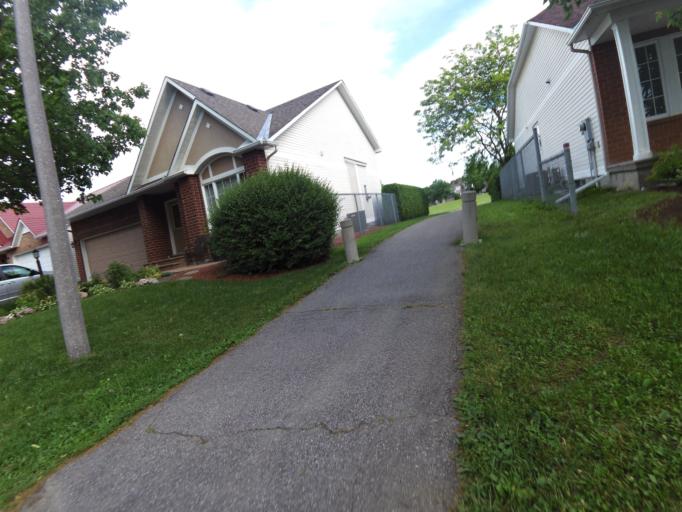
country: CA
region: Ontario
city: Bells Corners
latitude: 45.2799
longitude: -75.7169
